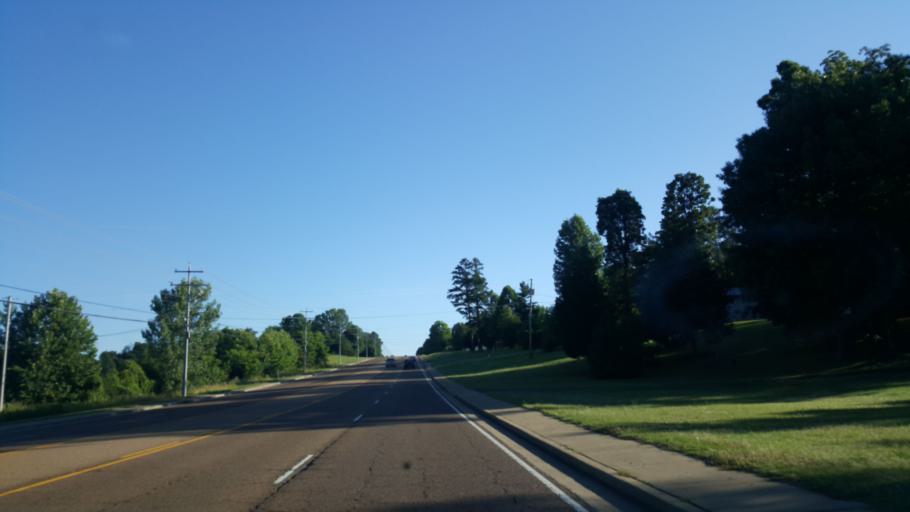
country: US
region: Tennessee
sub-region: Henderson County
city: Lexington
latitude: 35.6708
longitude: -88.3845
